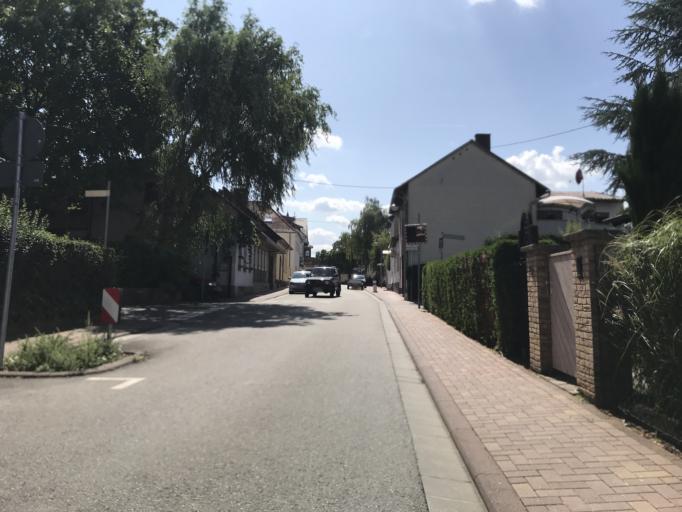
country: DE
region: Rheinland-Pfalz
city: Sprendlingen
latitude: 49.8636
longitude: 7.9875
